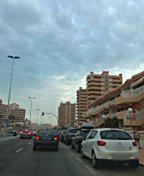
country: ES
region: Murcia
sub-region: Murcia
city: La Manga del Mar Menor
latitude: 37.6800
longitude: -0.7343
